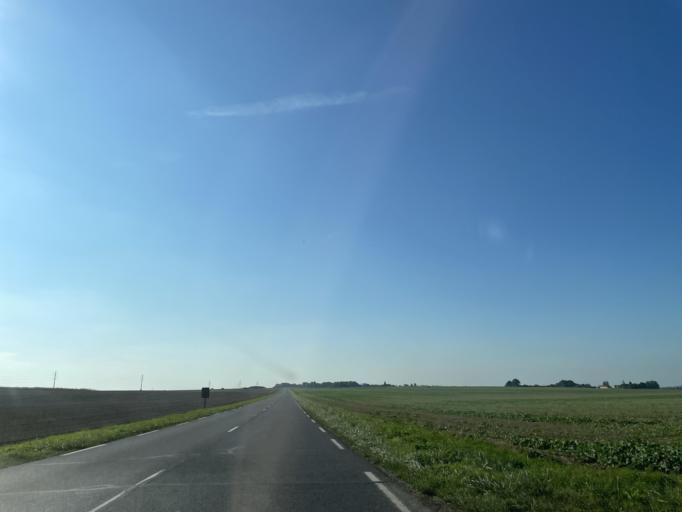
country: FR
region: Ile-de-France
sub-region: Departement de Seine-et-Marne
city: Chailly-en-Brie
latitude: 48.7876
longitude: 3.1465
